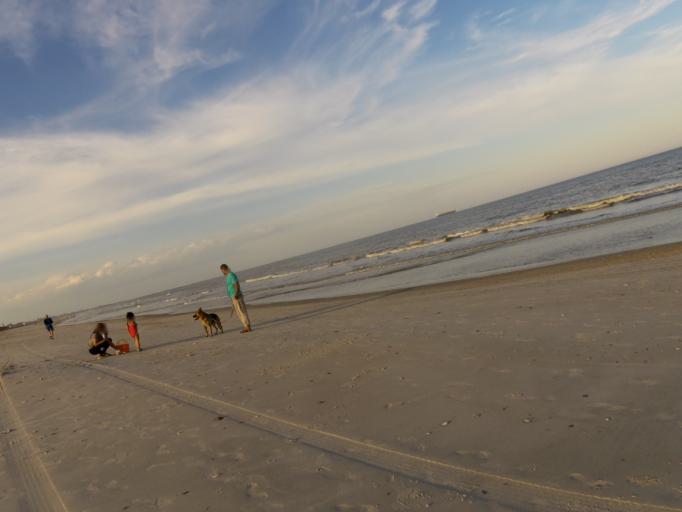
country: US
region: Florida
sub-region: Duval County
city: Atlantic Beach
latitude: 30.3728
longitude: -81.3973
